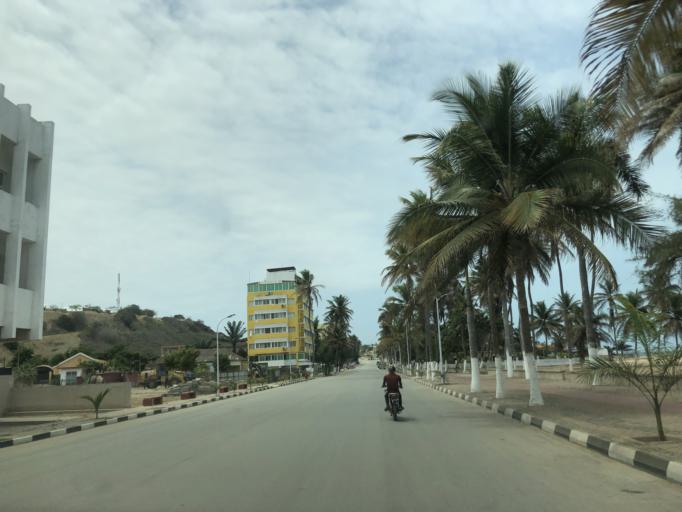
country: AO
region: Cuanza Sul
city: Sumbe
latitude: -11.1968
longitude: 13.8354
